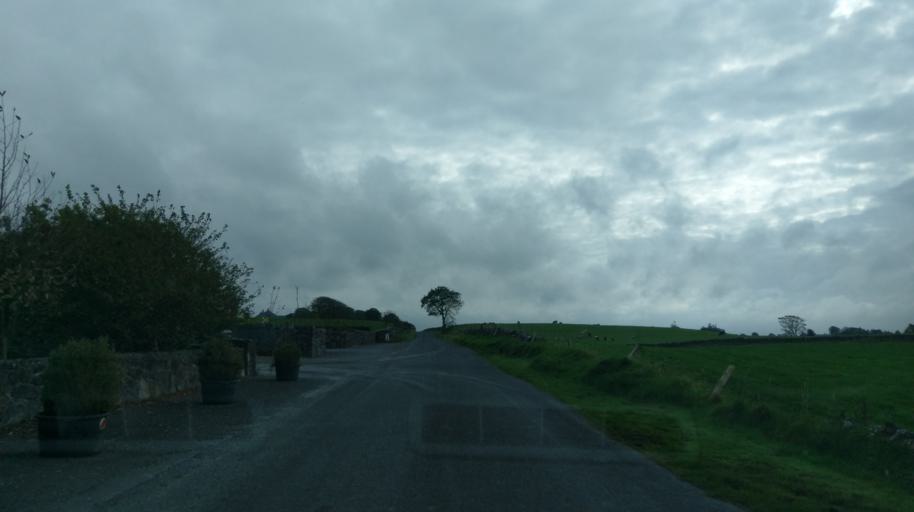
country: IE
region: Connaught
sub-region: County Galway
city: Athenry
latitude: 53.4588
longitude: -8.6171
